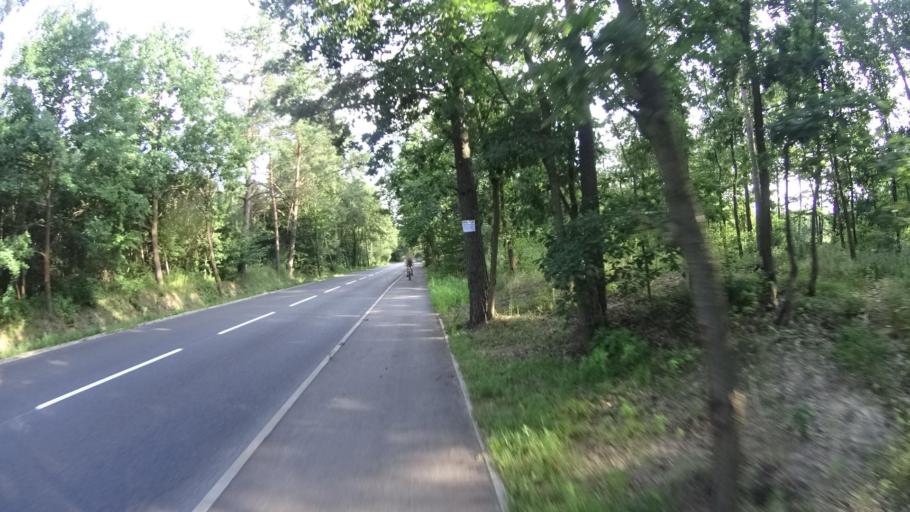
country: PL
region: Masovian Voivodeship
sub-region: Powiat piaseczynski
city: Tarczyn
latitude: 52.0268
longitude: 20.7838
